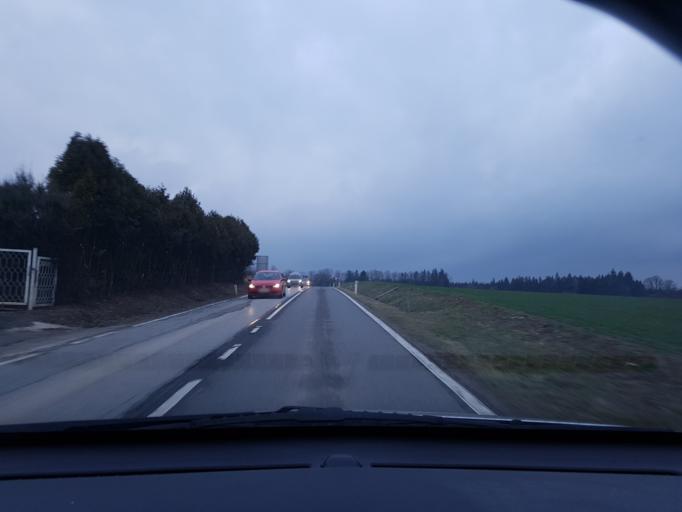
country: AT
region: Upper Austria
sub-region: Politischer Bezirk Steyr-Land
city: Sierning
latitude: 48.1209
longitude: 14.3471
